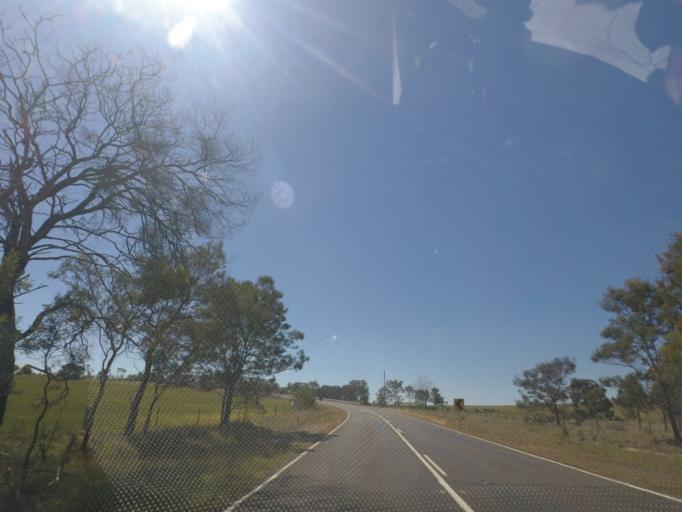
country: AU
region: Victoria
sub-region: Hume
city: Sunbury
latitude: -37.1235
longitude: 144.7689
